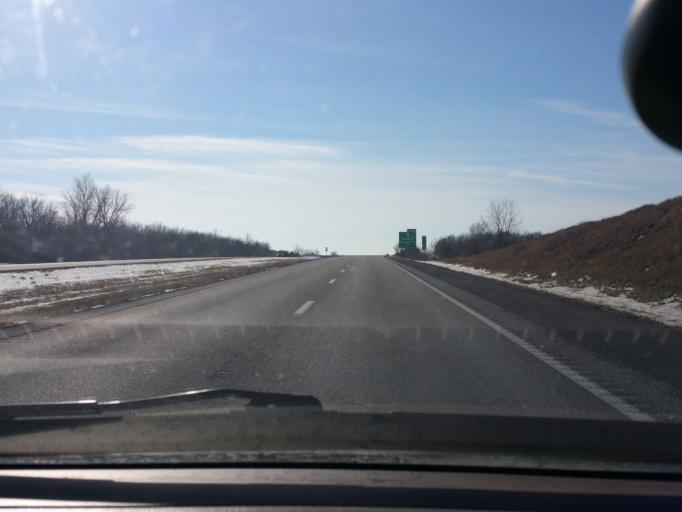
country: US
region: Missouri
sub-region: Daviess County
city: Gallatin
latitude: 39.9063
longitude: -94.1481
